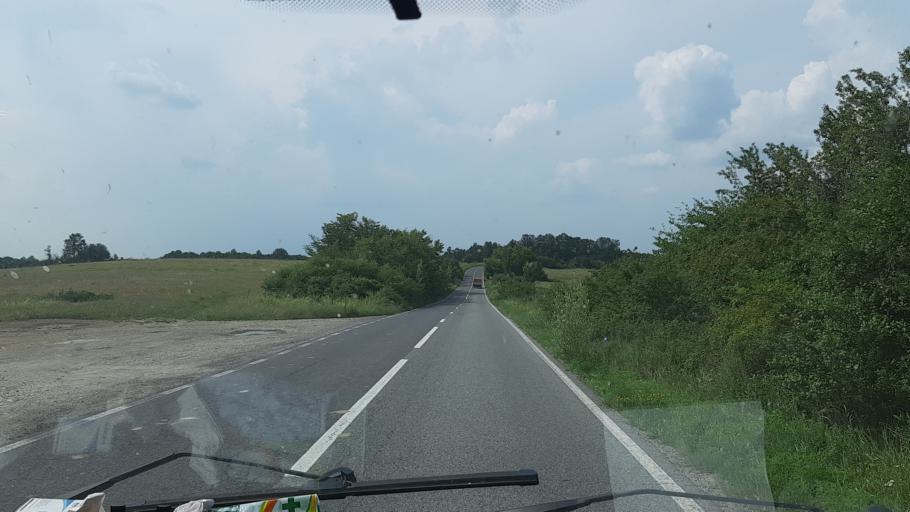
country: RO
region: Caras-Severin
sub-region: Comuna Farliug
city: Farliug
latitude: 45.5268
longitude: 21.8781
